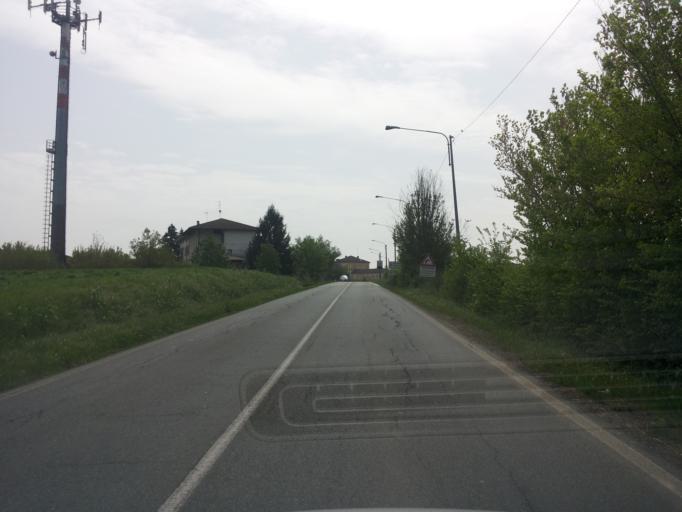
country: IT
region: Piedmont
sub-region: Provincia di Alessandria
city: Mirabello Monferrato
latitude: 45.0402
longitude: 8.5241
